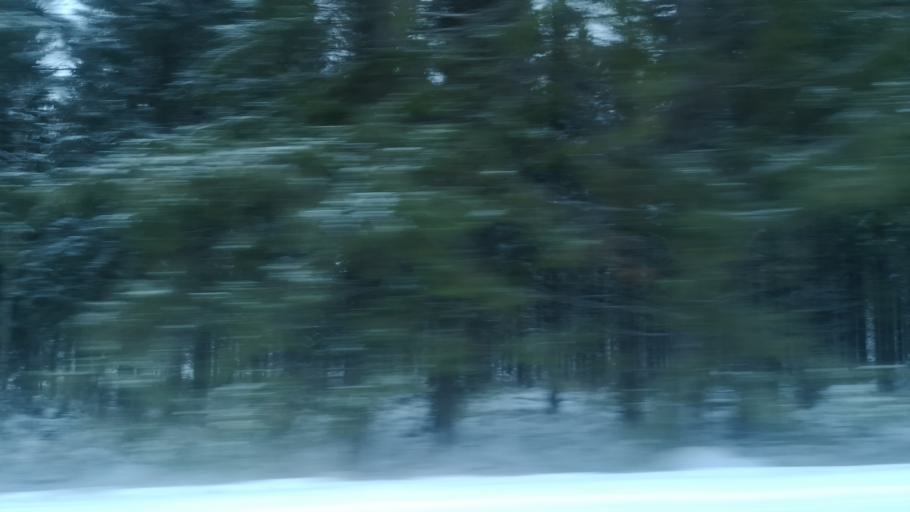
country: FI
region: Southern Savonia
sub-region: Savonlinna
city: Enonkoski
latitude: 62.0752
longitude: 28.7164
